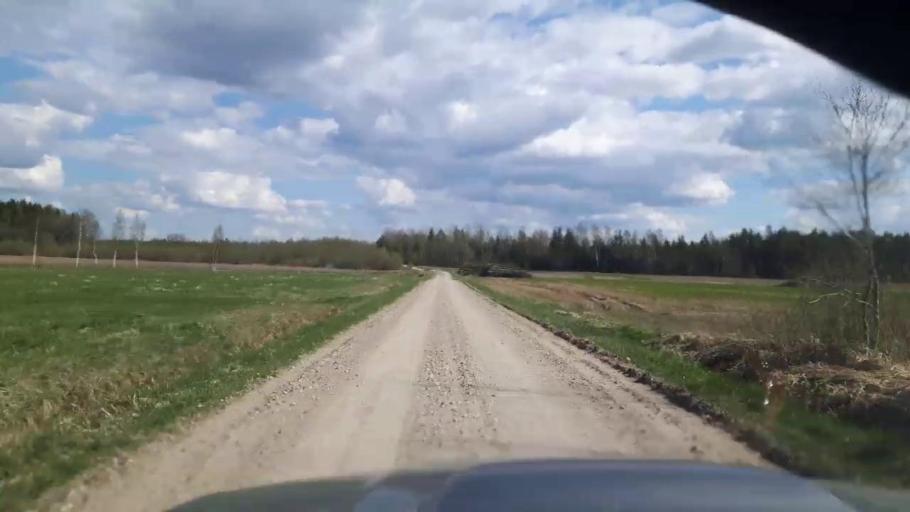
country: EE
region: Paernumaa
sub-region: Tootsi vald
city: Tootsi
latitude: 58.4474
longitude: 24.8392
